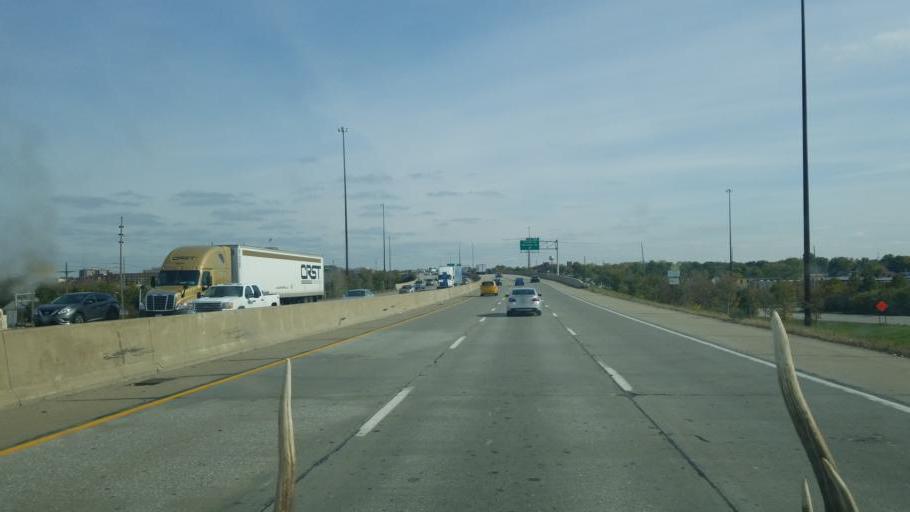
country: US
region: Indiana
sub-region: Marion County
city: Indianapolis
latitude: 39.7540
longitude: -86.1693
